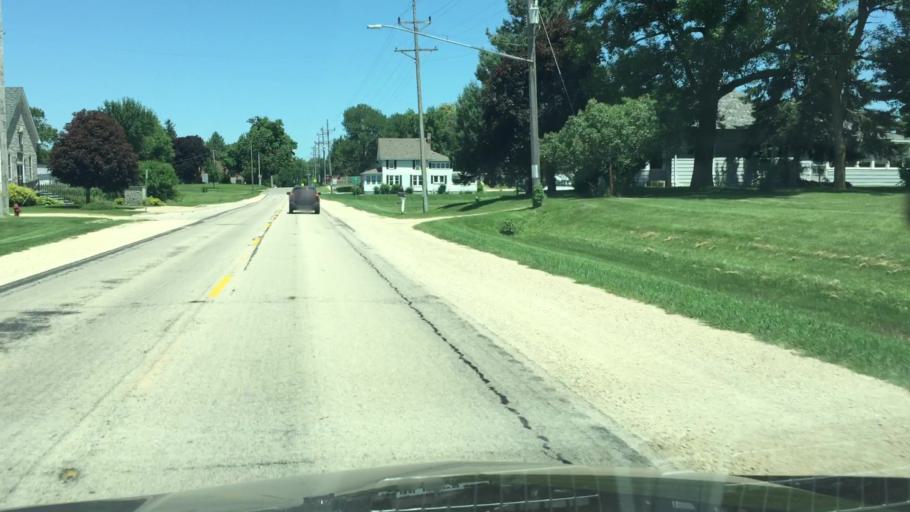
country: US
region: Iowa
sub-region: Cedar County
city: Mechanicsville
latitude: 41.9918
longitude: -91.1415
